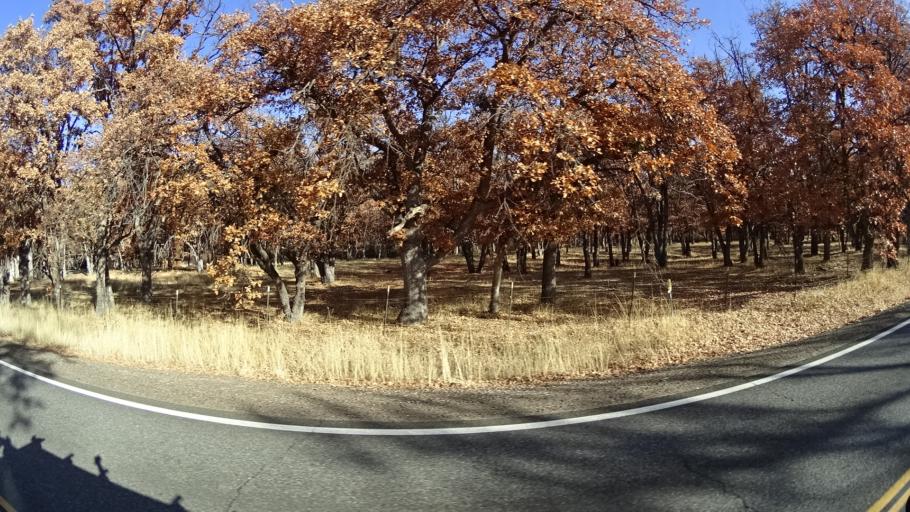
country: US
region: California
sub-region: Siskiyou County
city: Yreka
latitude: 41.6586
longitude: -122.5898
